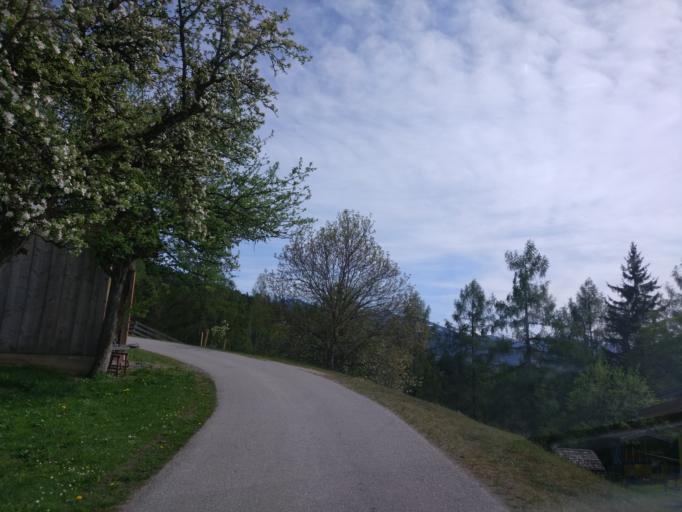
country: AT
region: Salzburg
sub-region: Politischer Bezirk Sankt Johann im Pongau
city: Pfarrwerfen
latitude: 47.4709
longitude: 13.2043
